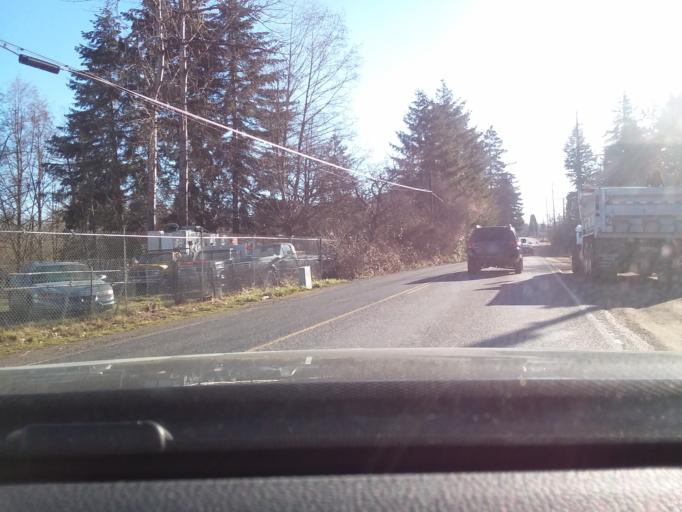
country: US
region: Washington
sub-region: Pierce County
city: Summit
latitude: 47.1399
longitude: -122.3624
